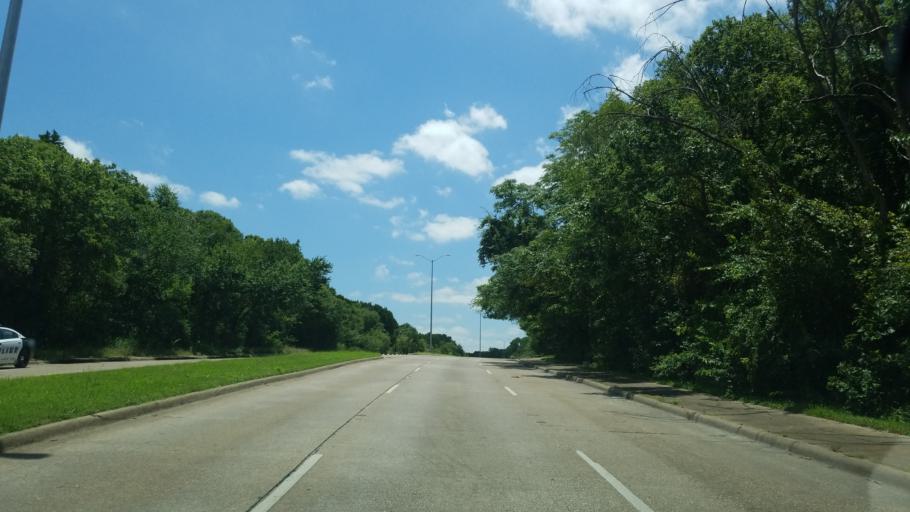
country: US
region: Texas
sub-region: Dallas County
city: Balch Springs
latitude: 32.7533
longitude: -96.7017
